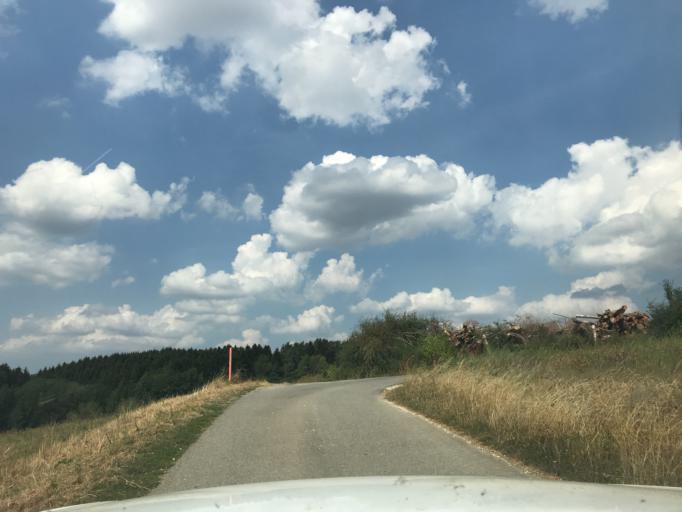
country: DE
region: Bavaria
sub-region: Upper Palatinate
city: Auerbach
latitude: 49.7328
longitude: 11.6310
